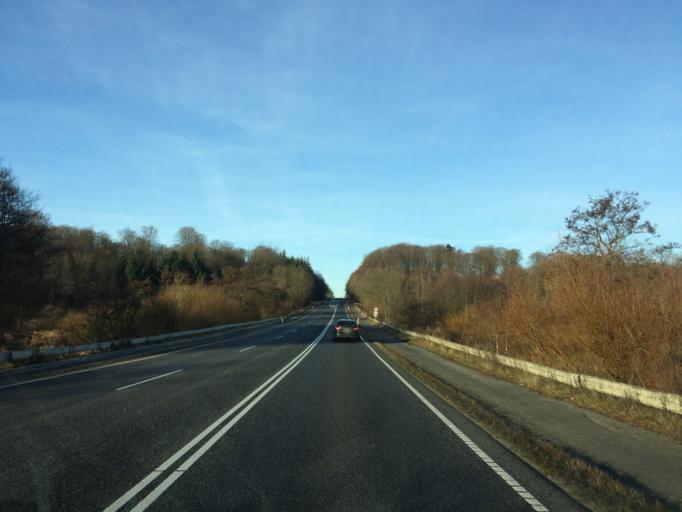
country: DK
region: South Denmark
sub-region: Vejle Kommune
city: Borkop
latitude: 55.5884
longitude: 9.6494
